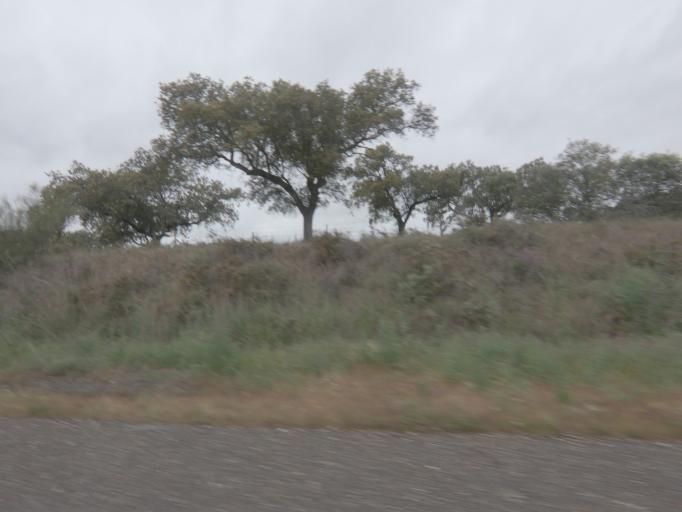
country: ES
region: Extremadura
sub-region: Provincia de Badajoz
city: La Roca de la Sierra
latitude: 39.0717
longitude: -6.7547
